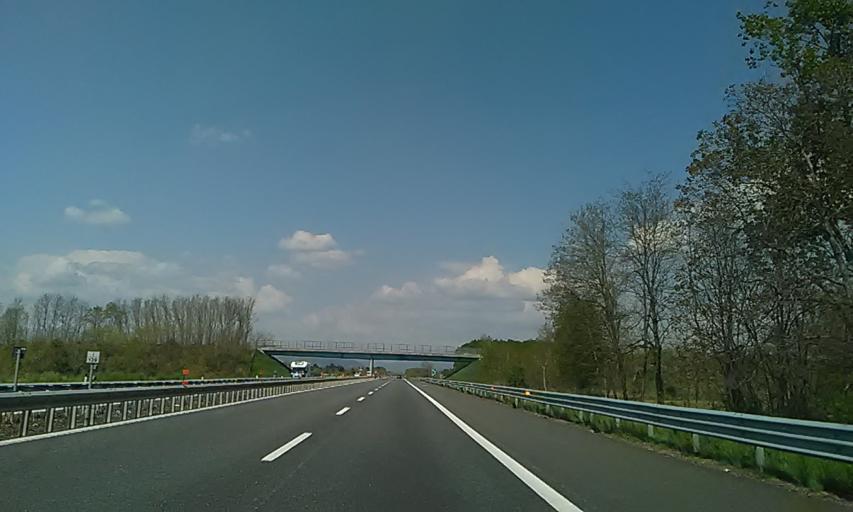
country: IT
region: Piedmont
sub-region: Provincia di Novara
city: Carpignano Sesia
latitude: 45.5570
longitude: 8.4192
